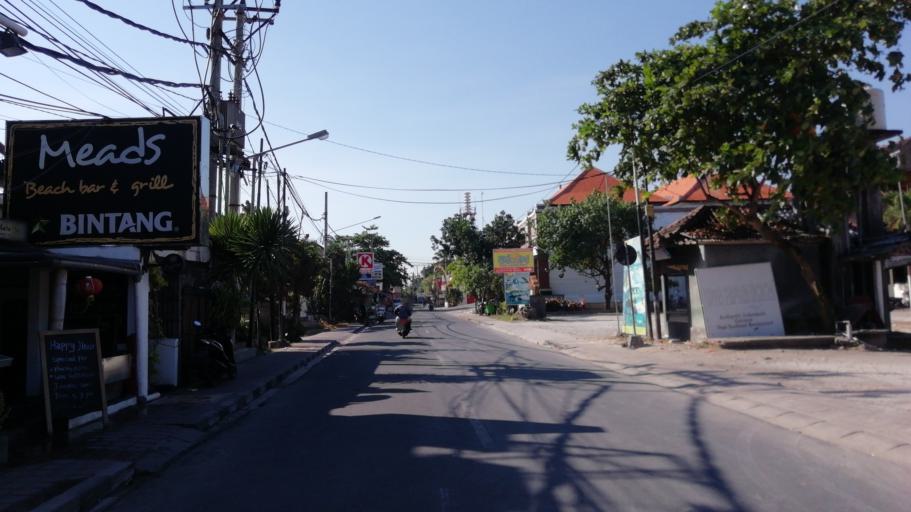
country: ID
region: Bali
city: Bualu
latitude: -8.7576
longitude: 115.2215
